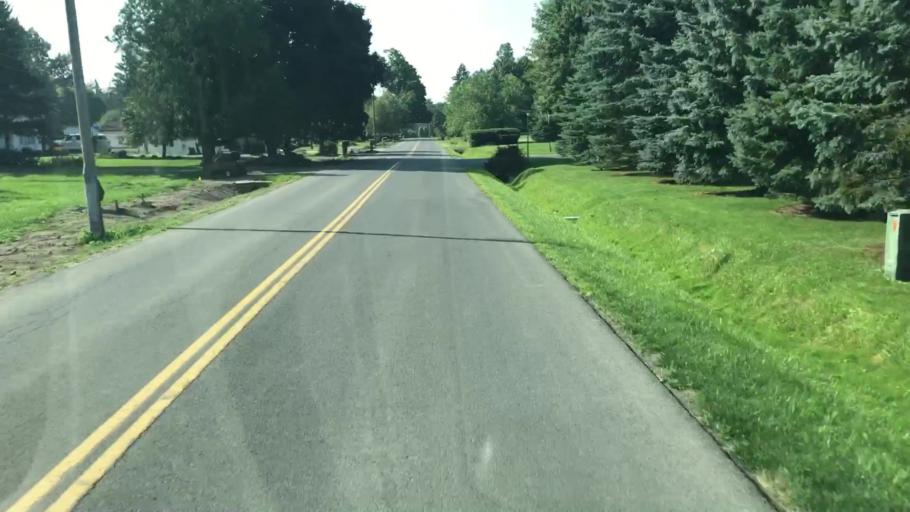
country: US
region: New York
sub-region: Cayuga County
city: Melrose Park
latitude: 42.9109
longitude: -76.5293
